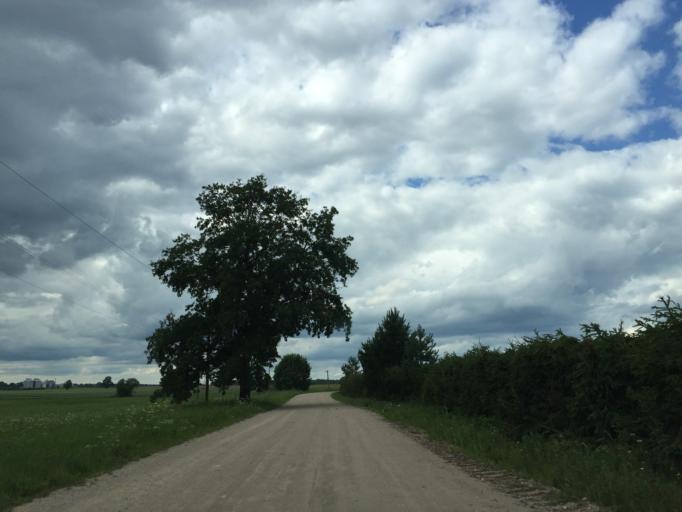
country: LV
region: Ogre
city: Jumprava
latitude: 56.8453
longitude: 25.0505
